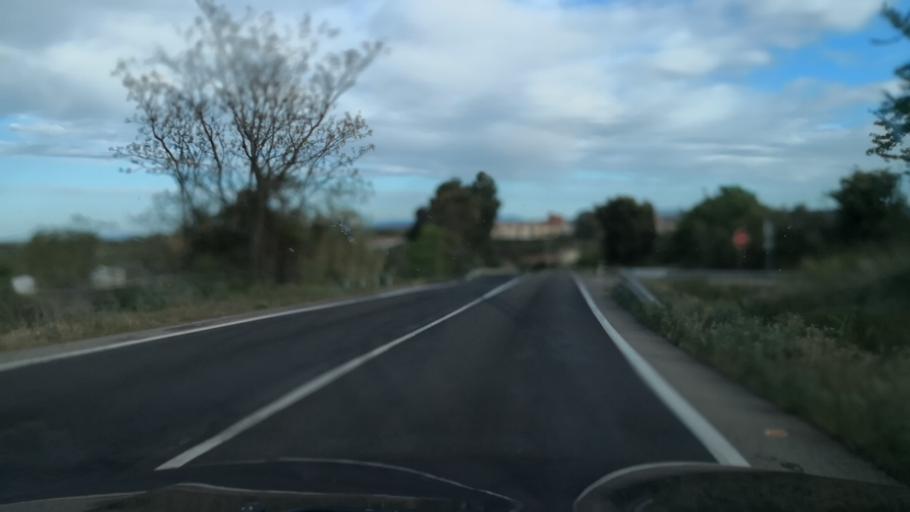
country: ES
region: Extremadura
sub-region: Provincia de Caceres
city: Coria
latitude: 39.9986
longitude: -6.5478
